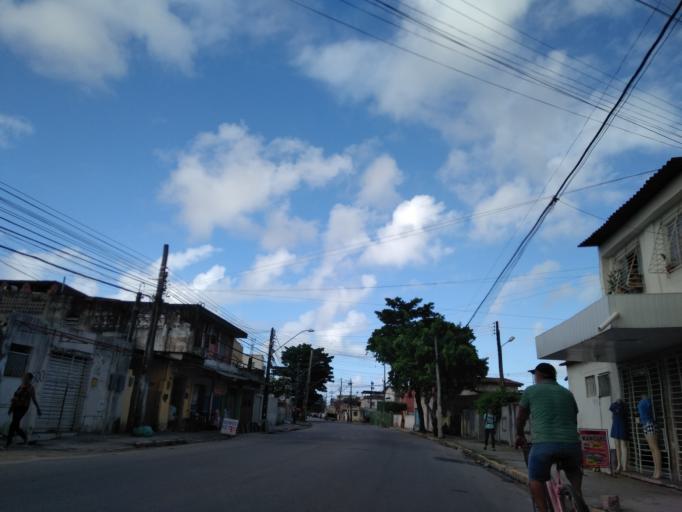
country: BR
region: Pernambuco
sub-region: Recife
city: Recife
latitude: -8.0748
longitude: -34.9208
